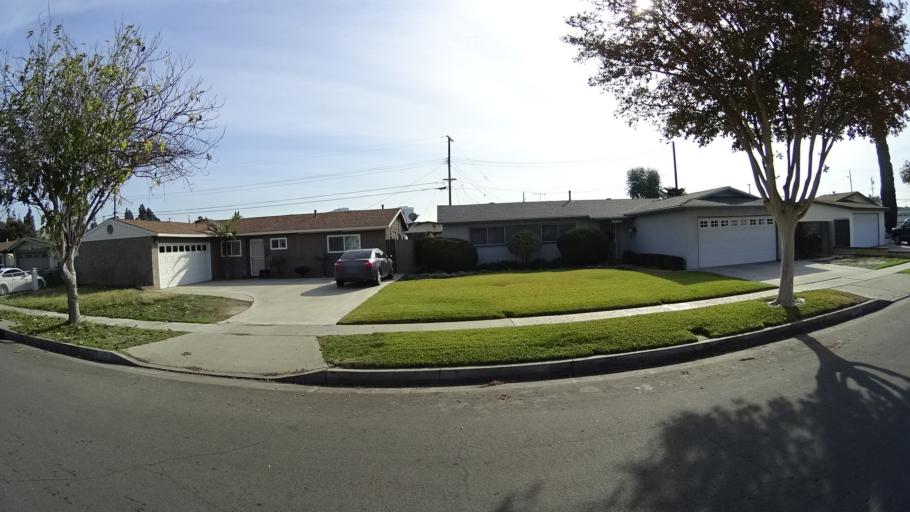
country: US
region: California
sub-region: Orange County
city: Garden Grove
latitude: 33.7852
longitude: -117.9025
